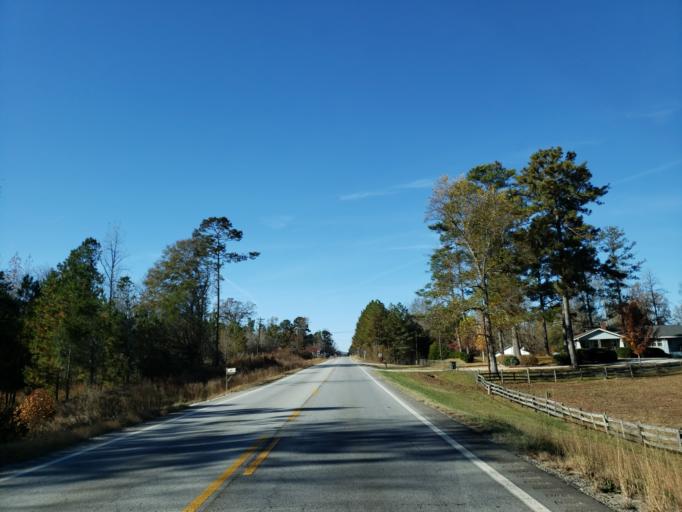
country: US
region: Alabama
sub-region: Calhoun County
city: Choccolocco
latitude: 33.5828
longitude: -85.6779
